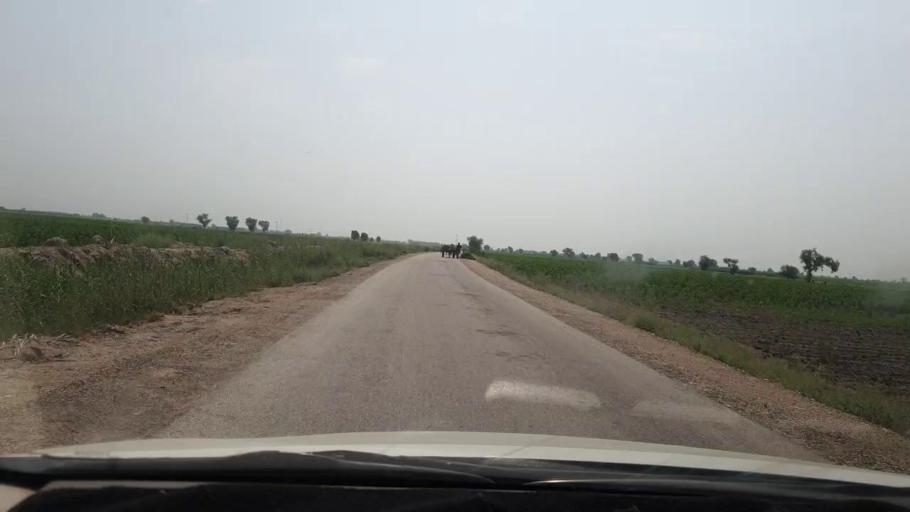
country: PK
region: Sindh
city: Rohri
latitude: 27.5379
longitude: 69.0003
